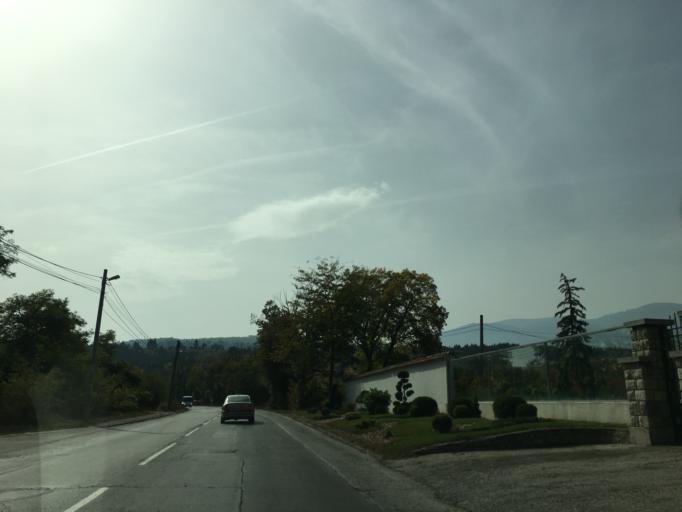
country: BG
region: Sofia-Capital
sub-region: Stolichna Obshtina
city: Sofia
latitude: 42.6139
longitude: 23.4002
